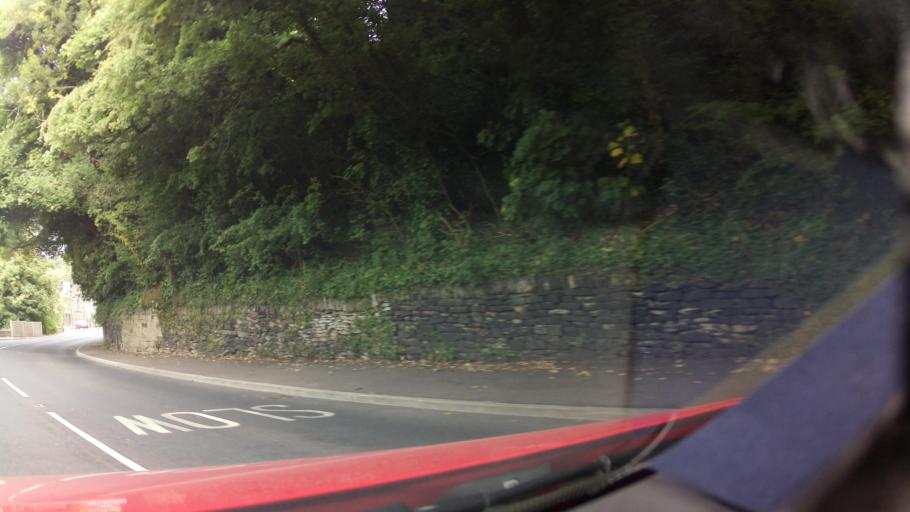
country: GB
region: England
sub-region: Kirklees
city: Holmfirth
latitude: 53.5745
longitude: -1.7533
